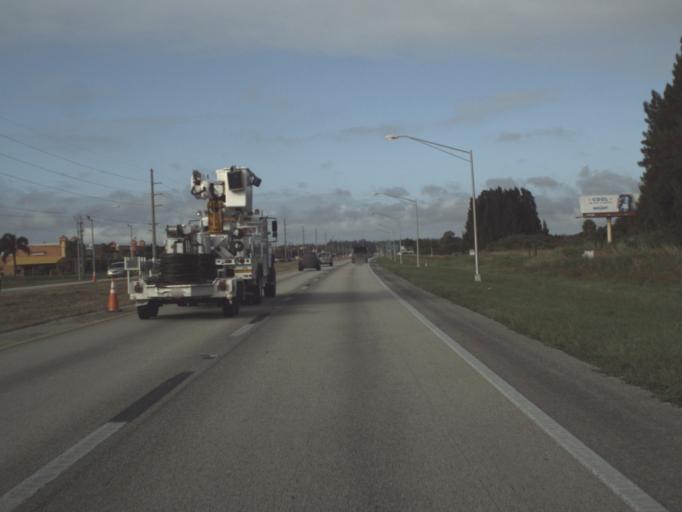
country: US
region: Florida
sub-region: Lee County
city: Lochmoor Waterway Estates
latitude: 26.6455
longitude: -81.9897
